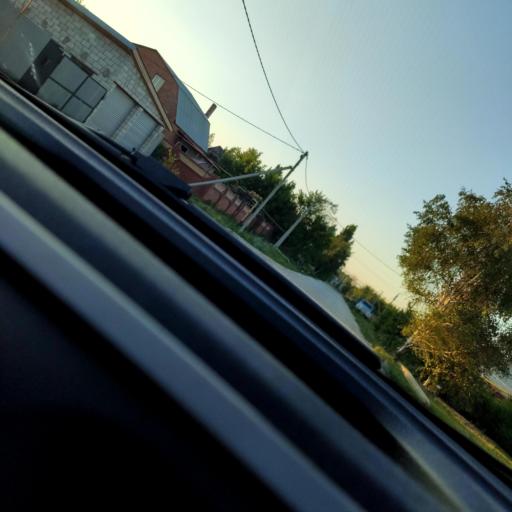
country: RU
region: Samara
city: Tol'yatti
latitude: 53.5536
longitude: 49.4041
